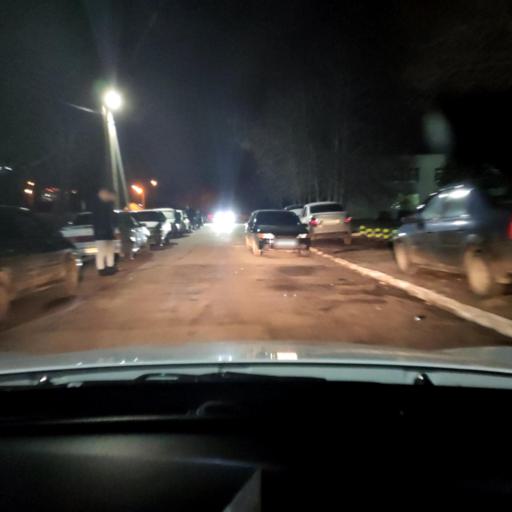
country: RU
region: Tatarstan
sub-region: Gorod Kazan'
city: Kazan
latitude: 55.7185
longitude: 49.1635
